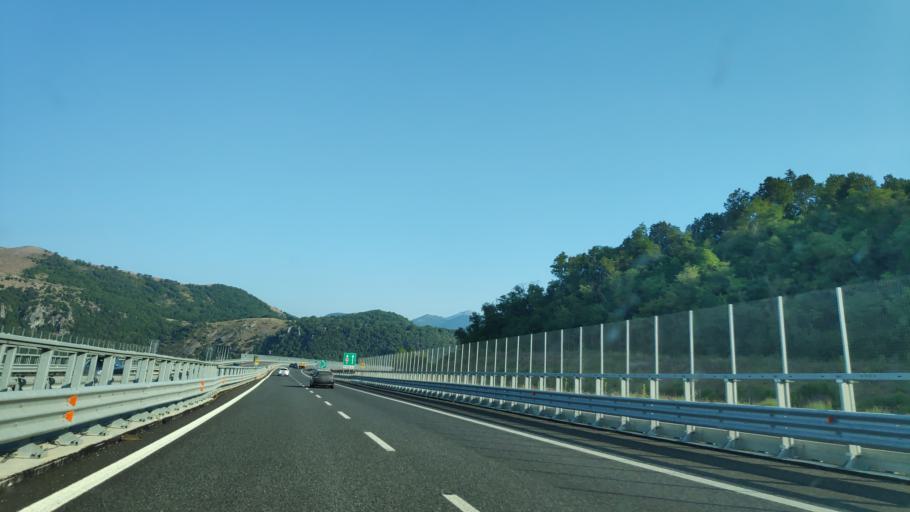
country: IT
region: Calabria
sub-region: Provincia di Cosenza
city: Laino Castello-Nuovo Centro
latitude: 39.9317
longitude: 15.9632
